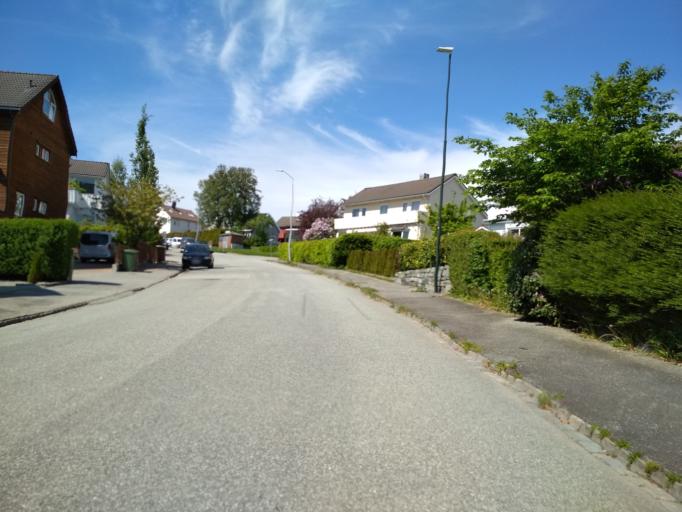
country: NO
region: Rogaland
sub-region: Stavanger
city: Stavanger
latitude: 58.9557
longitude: 5.7339
